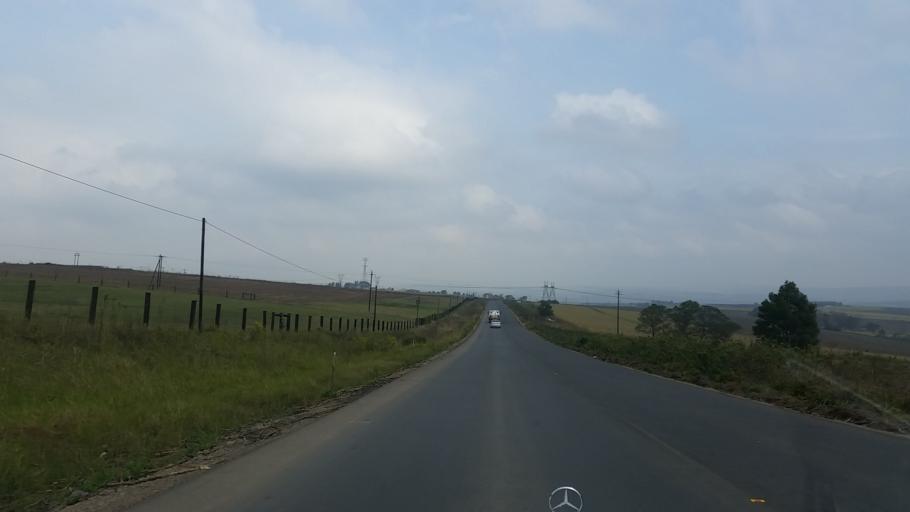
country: ZA
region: KwaZulu-Natal
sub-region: uMgungundlovu District Municipality
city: Camperdown
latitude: -29.7602
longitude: 30.5072
